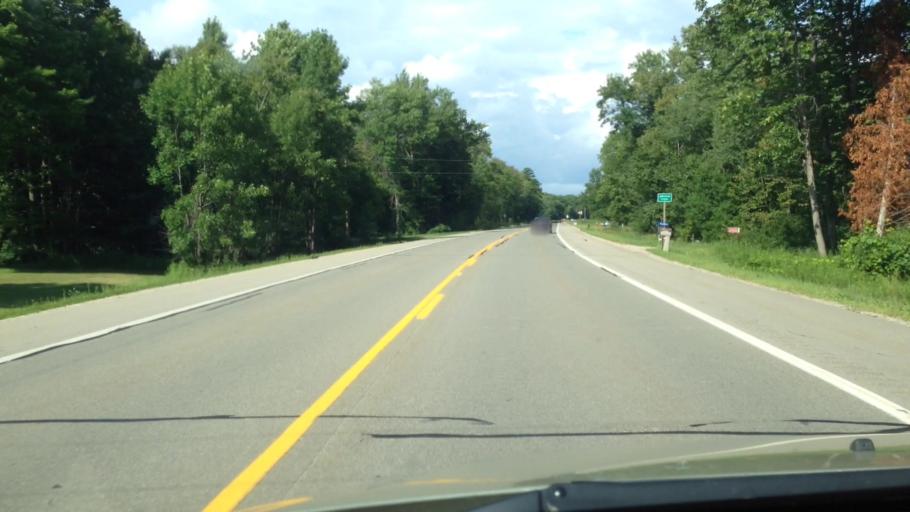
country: US
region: Michigan
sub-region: Menominee County
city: Menominee
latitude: 45.2736
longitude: -87.4668
